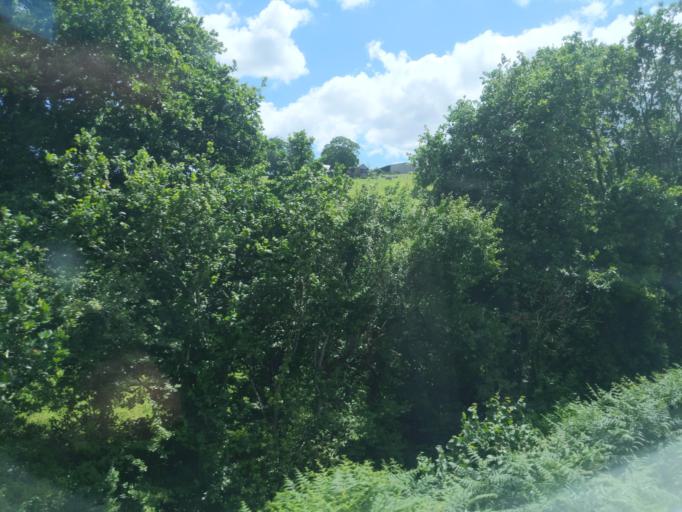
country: GB
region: England
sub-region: Cornwall
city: Lostwithiel
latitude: 50.3857
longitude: -4.6716
